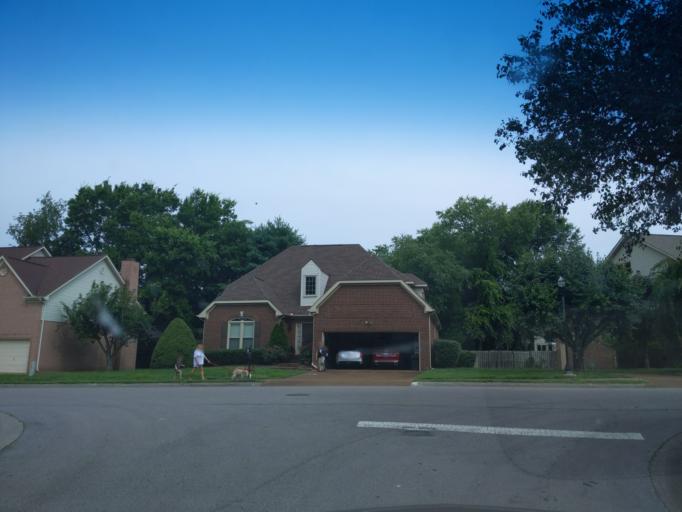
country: US
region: Tennessee
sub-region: Williamson County
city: Brentwood Estates
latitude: 36.0342
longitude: -86.7620
